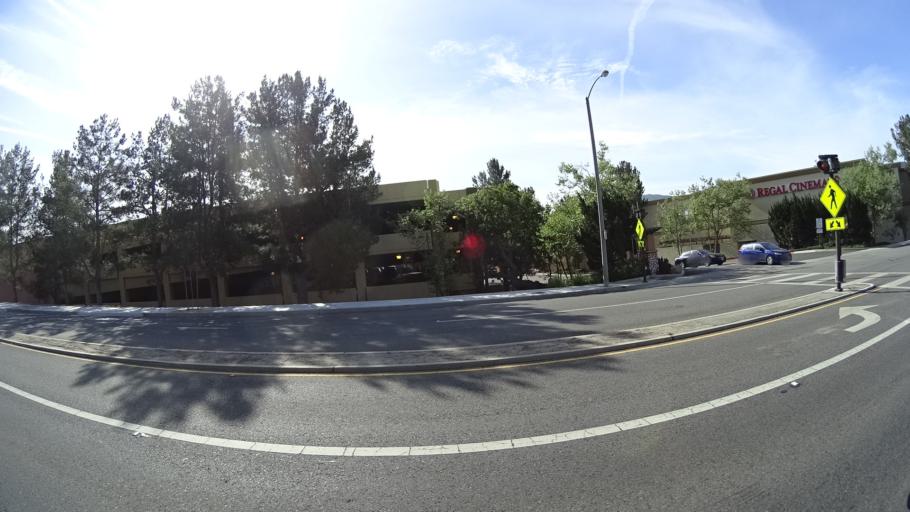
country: US
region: California
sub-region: Ventura County
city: Thousand Oaks
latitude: 34.1837
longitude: -118.8792
